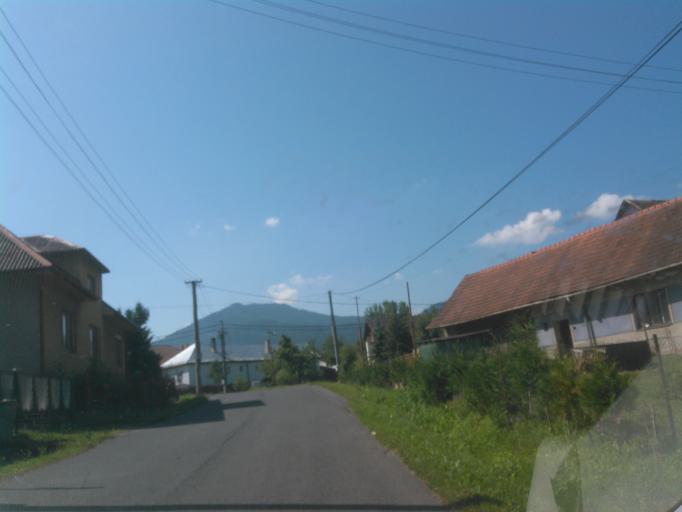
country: SK
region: Zilinsky
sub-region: Okres Liptovsky Mikulas
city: Liptovsky Mikulas
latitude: 49.0385
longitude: 19.4997
